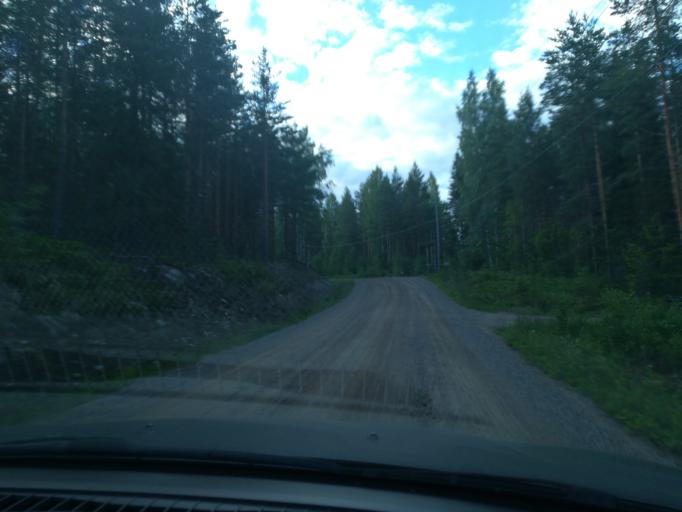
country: FI
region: Southern Savonia
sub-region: Mikkeli
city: Puumala
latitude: 61.6027
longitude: 28.1503
